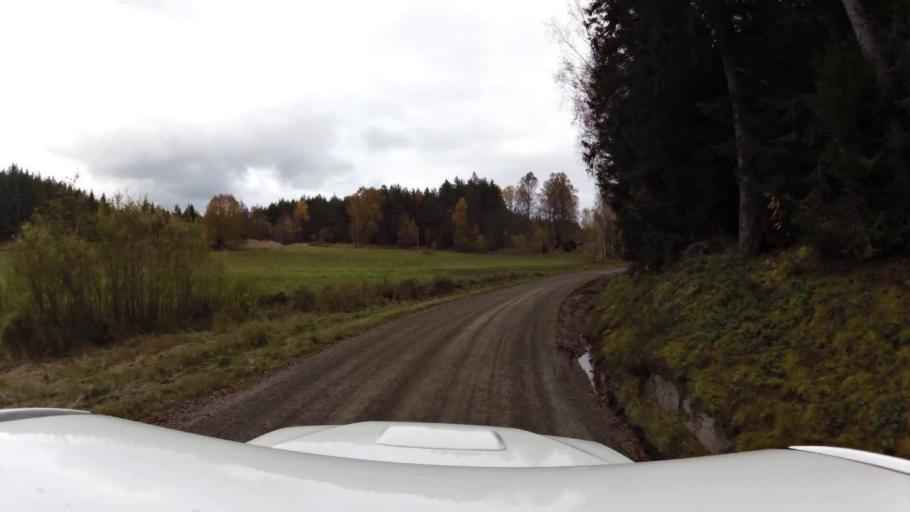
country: SE
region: OEstergoetland
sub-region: Linkopings Kommun
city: Ljungsbro
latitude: 58.5805
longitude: 15.4423
